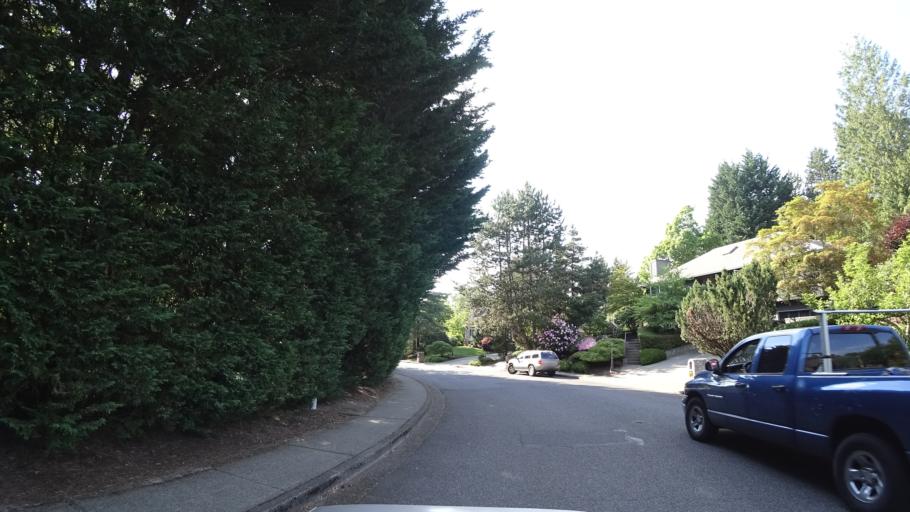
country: US
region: Oregon
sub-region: Washington County
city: Garden Home-Whitford
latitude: 45.4614
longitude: -122.7398
